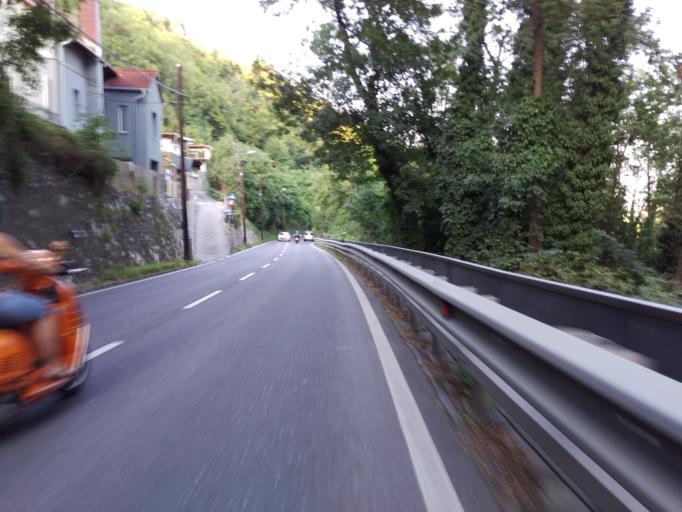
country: AT
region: Styria
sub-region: Graz Stadt
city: Wetzelsdorf
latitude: 47.0601
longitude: 15.3782
